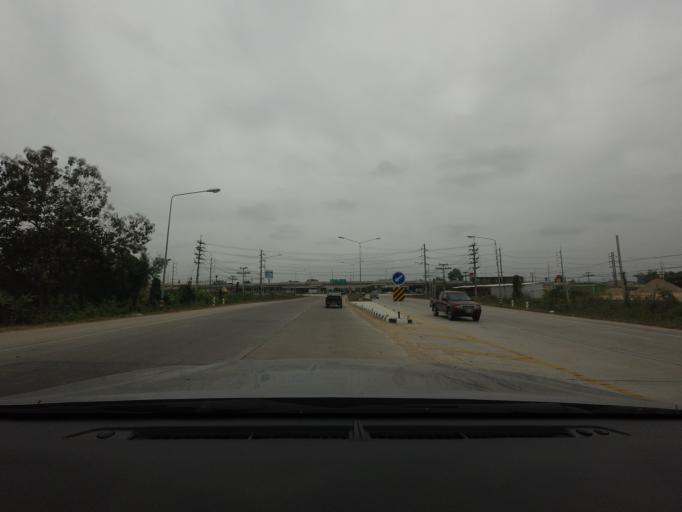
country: TH
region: Lamphun
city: Lamphun
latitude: 18.6141
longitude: 99.0433
